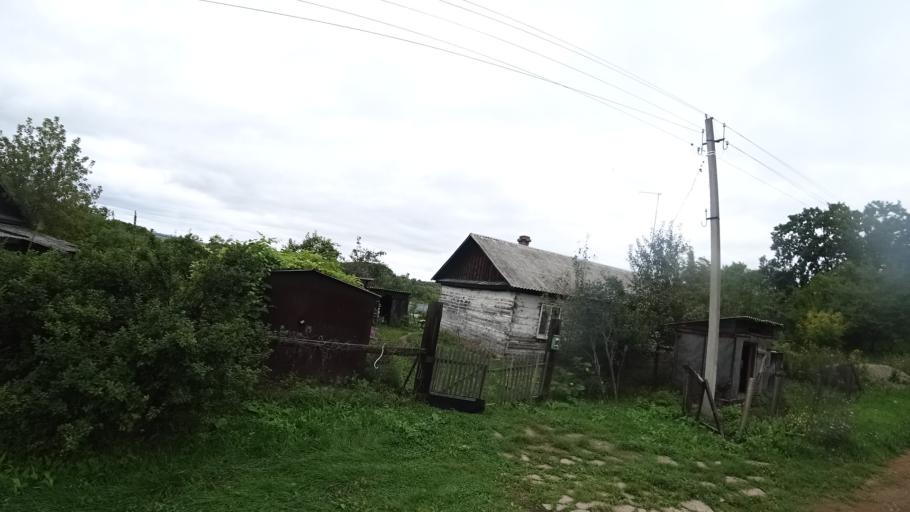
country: RU
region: Primorskiy
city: Chernigovka
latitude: 44.4527
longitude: 132.5935
